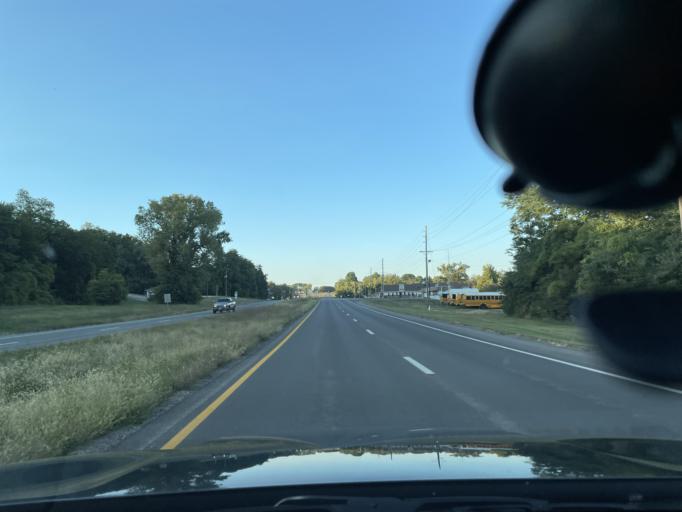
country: US
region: Missouri
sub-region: Andrew County
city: Country Club Village
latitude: 39.8080
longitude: -94.8408
